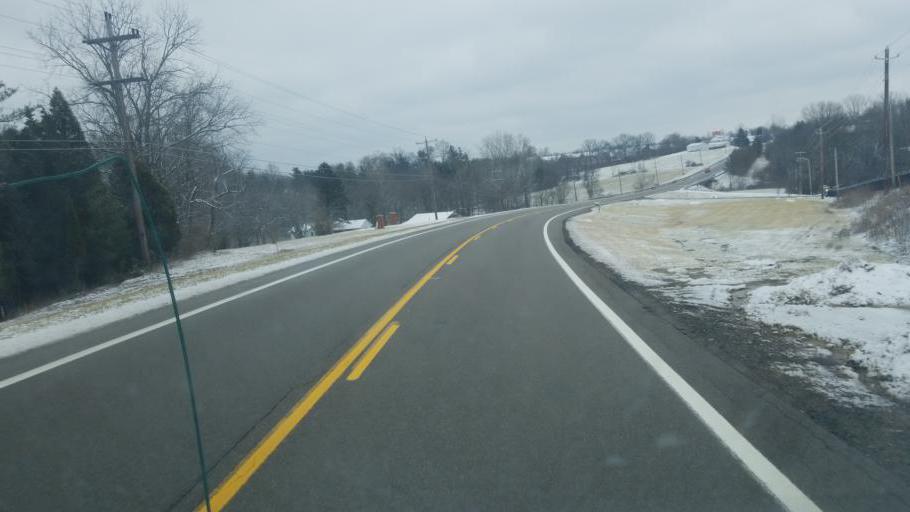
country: US
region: Ohio
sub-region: Licking County
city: Johnstown
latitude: 40.1652
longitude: -82.6967
